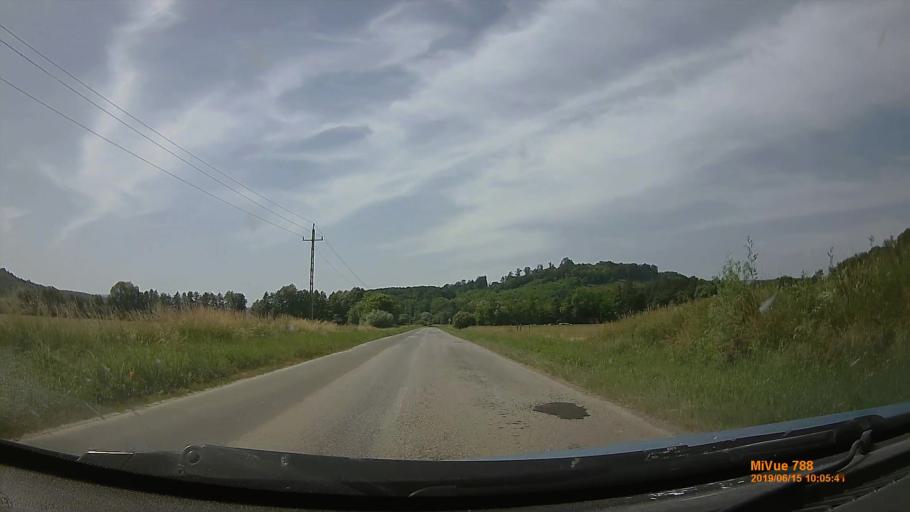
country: HU
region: Baranya
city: Sasd
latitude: 46.1896
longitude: 18.0825
